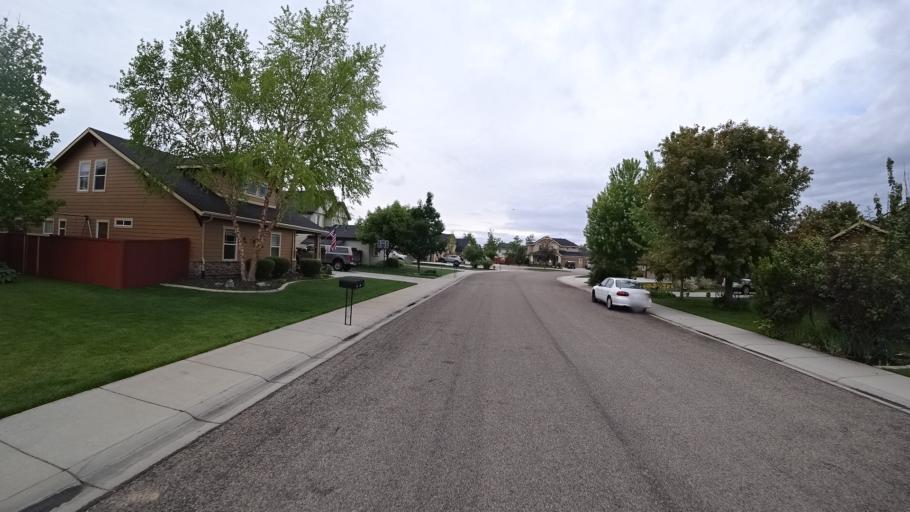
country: US
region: Idaho
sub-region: Ada County
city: Star
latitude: 43.7003
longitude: -116.4786
